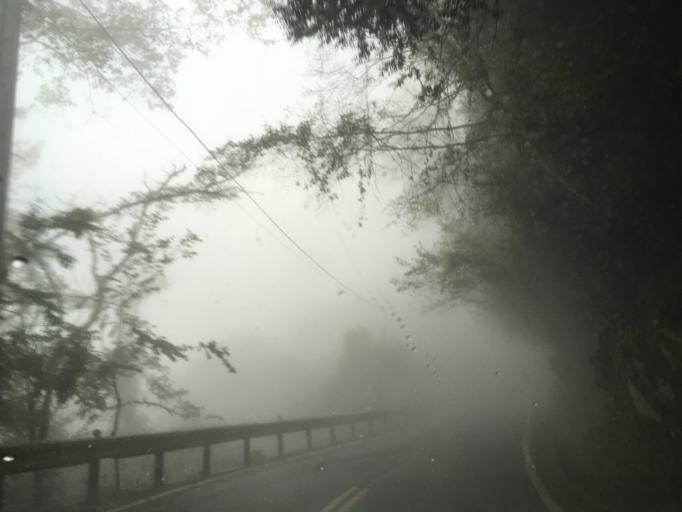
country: TW
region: Taiwan
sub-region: Hualien
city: Hualian
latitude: 24.1927
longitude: 121.4188
